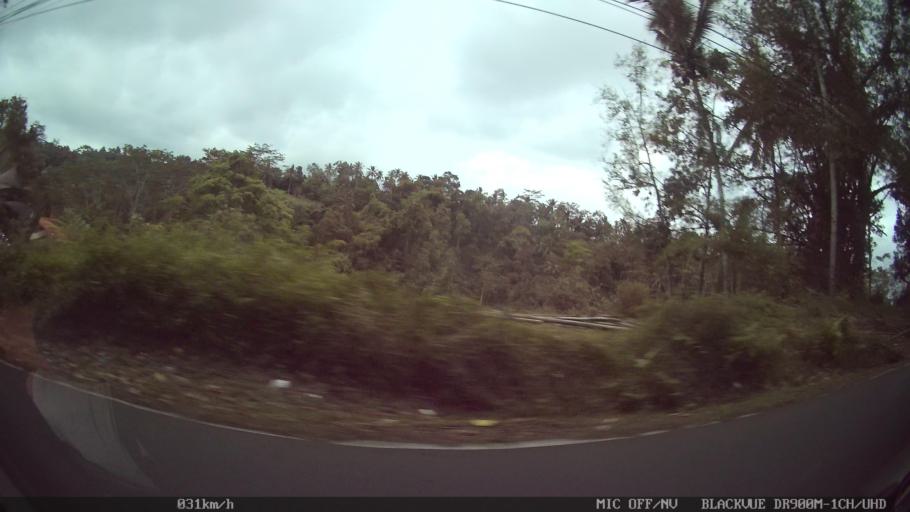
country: ID
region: Bali
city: Banjar Triwangsakeliki
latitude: -8.4474
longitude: 115.2695
